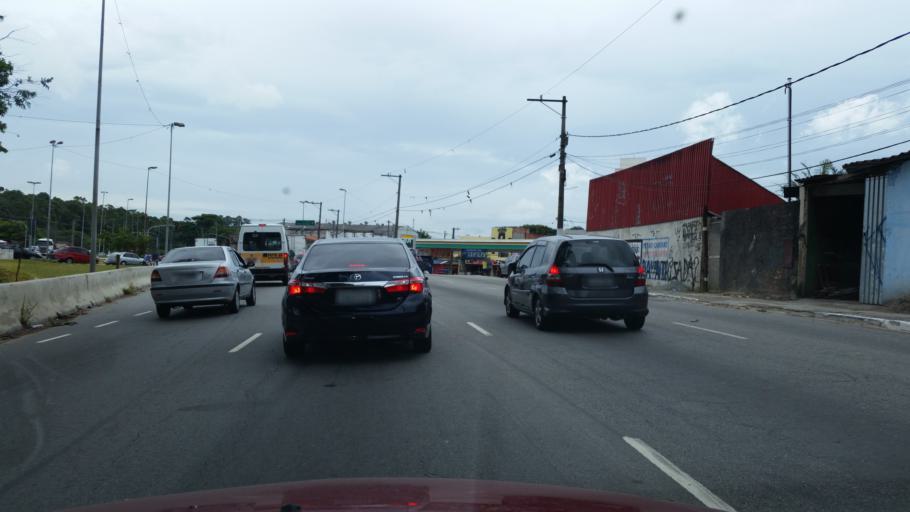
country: BR
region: Sao Paulo
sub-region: Guarulhos
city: Guarulhos
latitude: -23.5066
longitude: -46.4563
